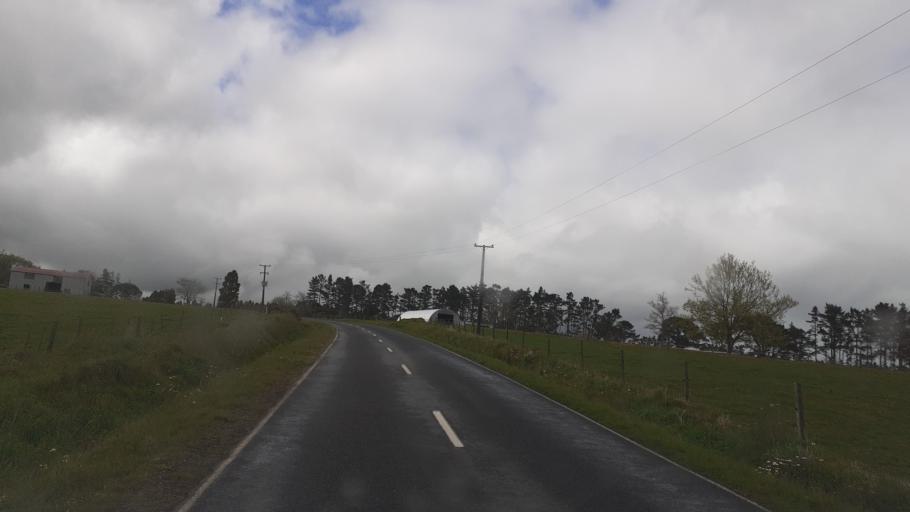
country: NZ
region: Northland
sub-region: Far North District
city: Waimate North
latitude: -35.2509
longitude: 173.7966
